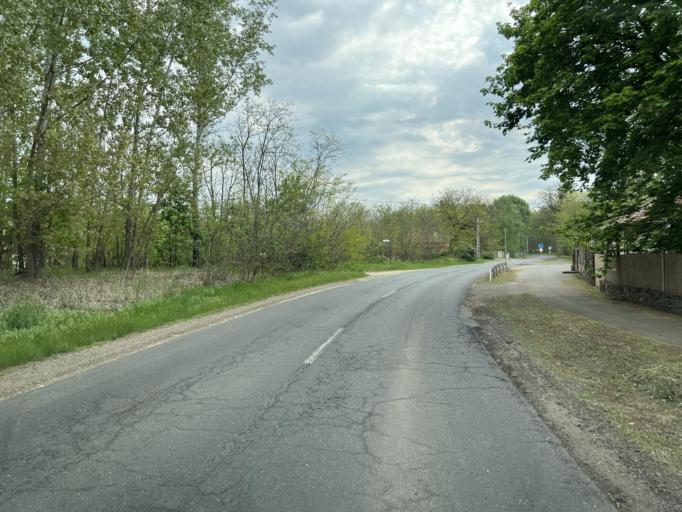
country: HU
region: Pest
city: Farmos
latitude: 47.3818
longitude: 19.8844
